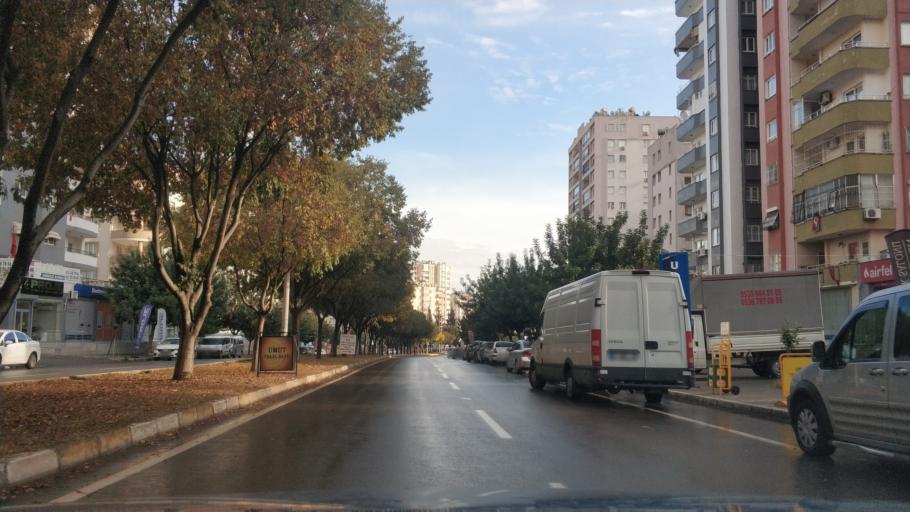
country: TR
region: Adana
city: Seyhan
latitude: 37.0394
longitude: 35.2766
